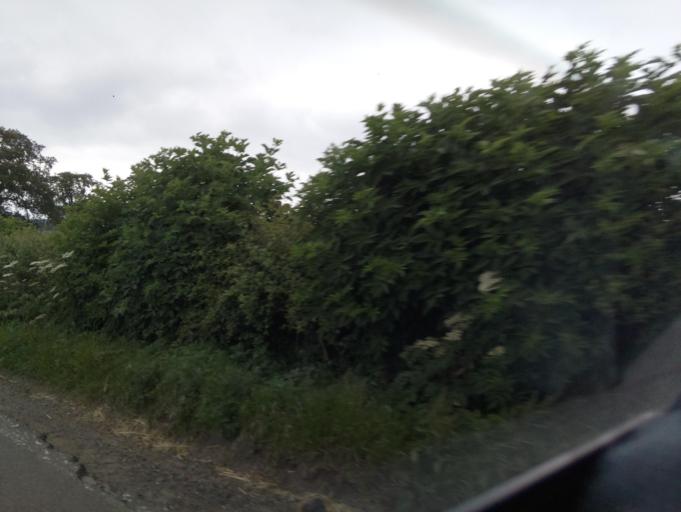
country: GB
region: England
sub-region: Derbyshire
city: Rodsley
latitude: 52.9134
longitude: -1.7607
